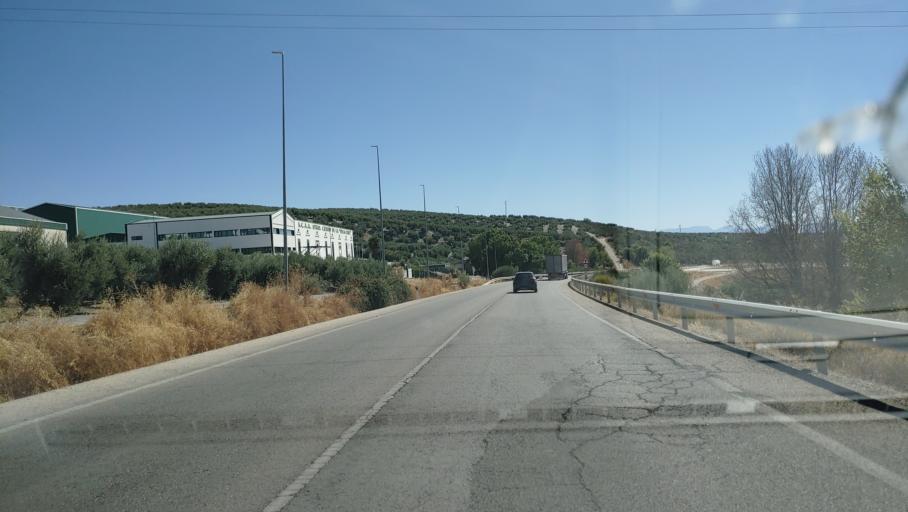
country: ES
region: Andalusia
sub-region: Provincia de Jaen
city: Villacarrillo
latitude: 38.1085
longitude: -3.0991
